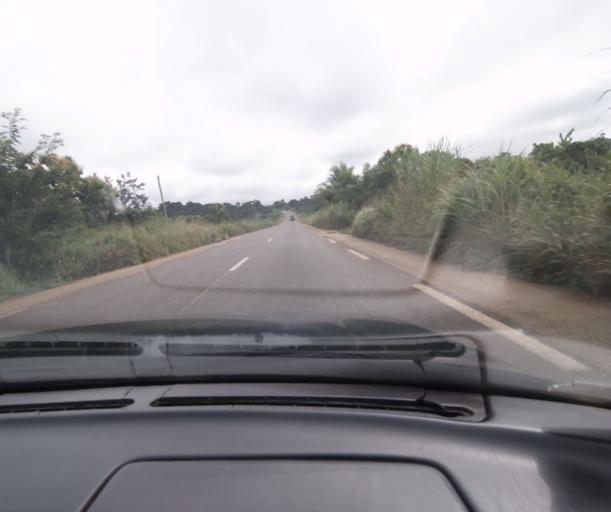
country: CM
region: Centre
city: Ombesa
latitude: 4.5670
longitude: 11.2651
